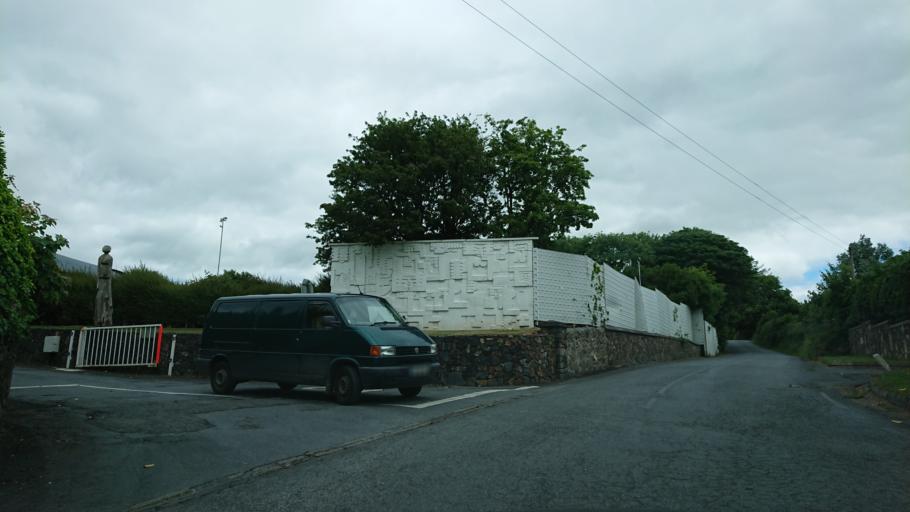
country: IE
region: Munster
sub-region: Waterford
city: Waterford
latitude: 52.2216
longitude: -7.1267
